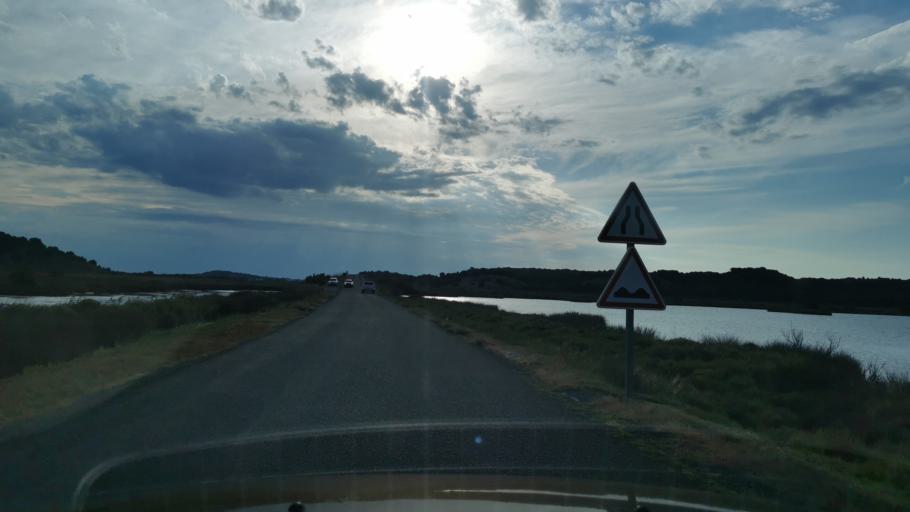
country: FR
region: Languedoc-Roussillon
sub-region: Departement de l'Aude
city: Gruissan
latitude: 43.1107
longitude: 3.0543
